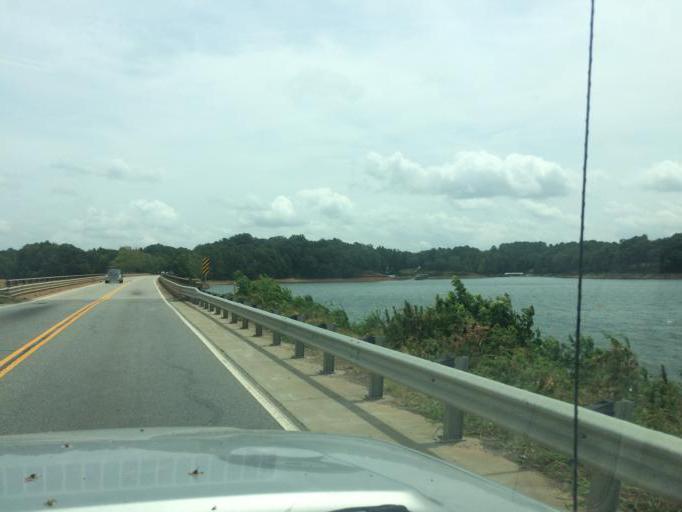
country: US
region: South Carolina
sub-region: Anderson County
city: Centerville
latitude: 34.5264
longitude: -82.7854
